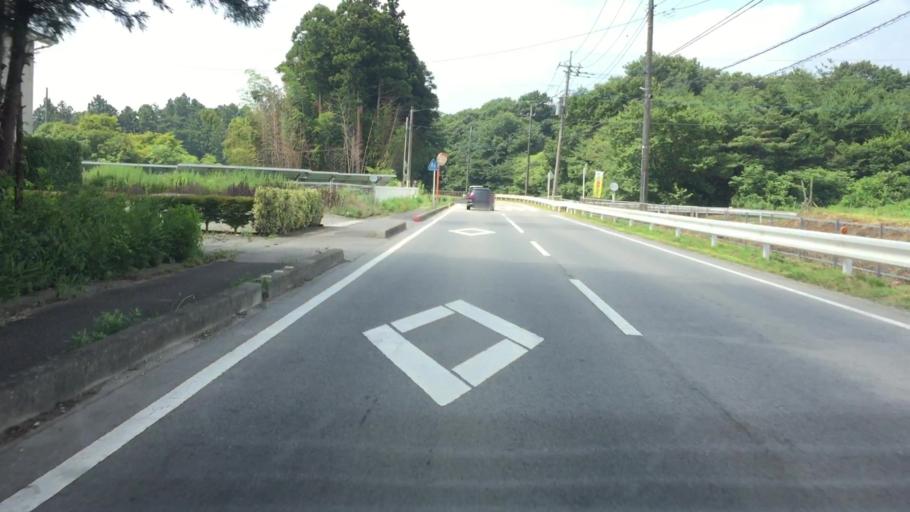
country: JP
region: Tochigi
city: Kuroiso
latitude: 37.0084
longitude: 140.0003
